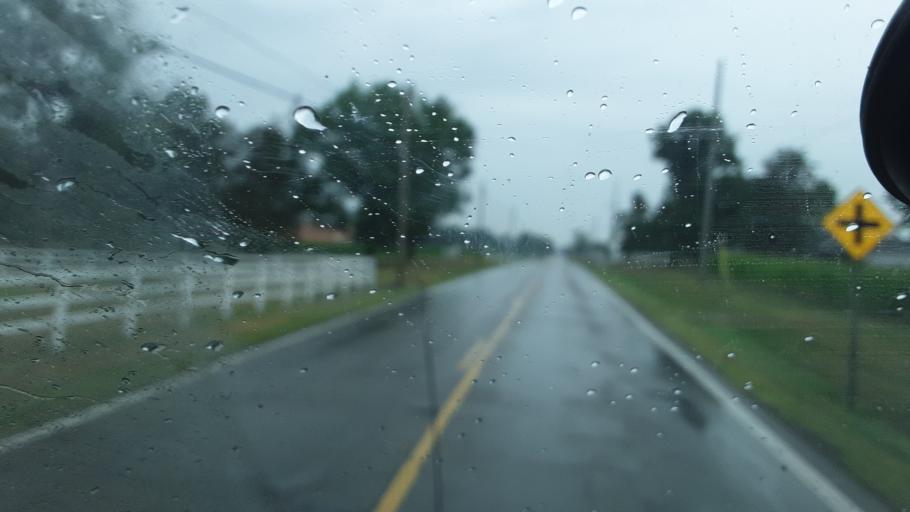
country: US
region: Ohio
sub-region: Williams County
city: Montpelier
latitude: 41.5553
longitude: -84.6131
